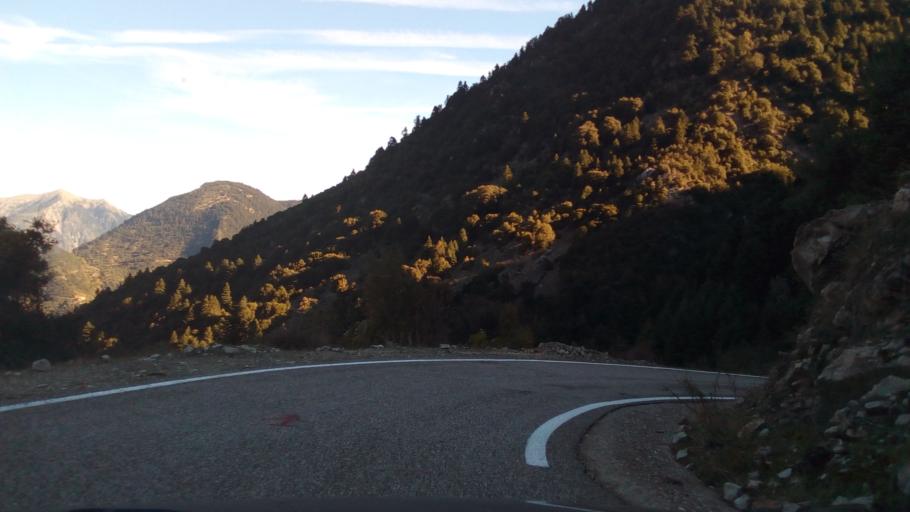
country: GR
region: West Greece
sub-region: Nomos Aitolias kai Akarnanias
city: Nafpaktos
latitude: 38.5419
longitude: 21.8517
